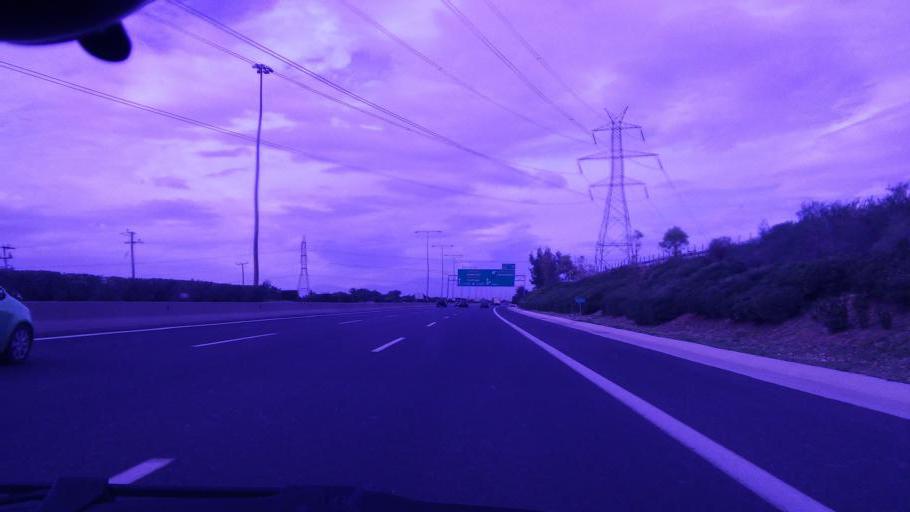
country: GR
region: Attica
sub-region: Nomarchia Dytikis Attikis
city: Fyli
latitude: 38.0870
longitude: 23.6393
